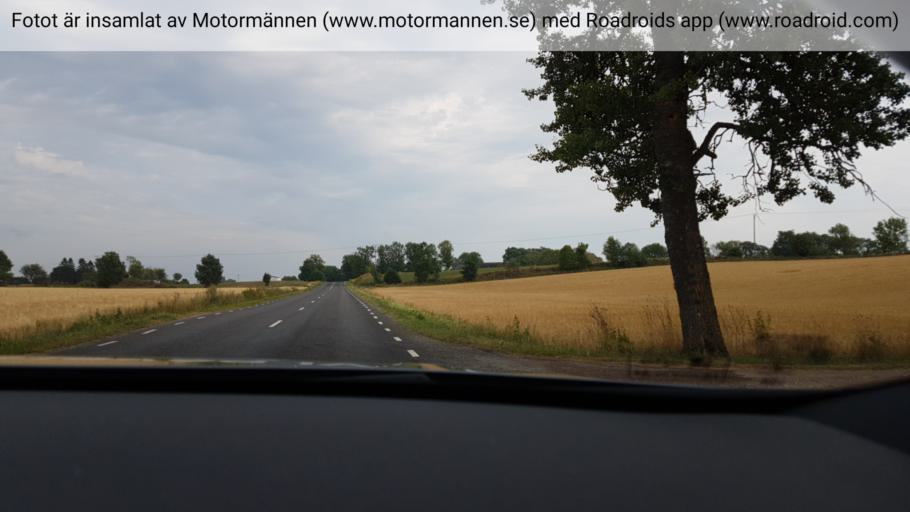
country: SE
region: Vaestra Goetaland
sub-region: Falkopings Kommun
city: Akarp
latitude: 58.1930
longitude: 13.6205
